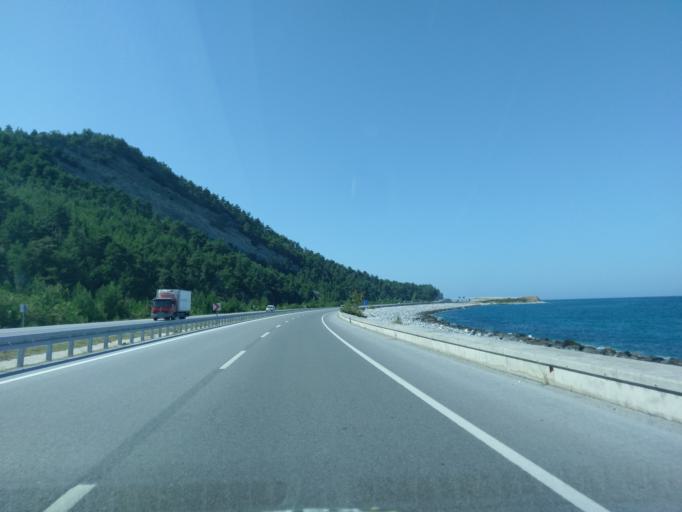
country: TR
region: Samsun
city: Yakakent
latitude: 41.6733
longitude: 35.4225
